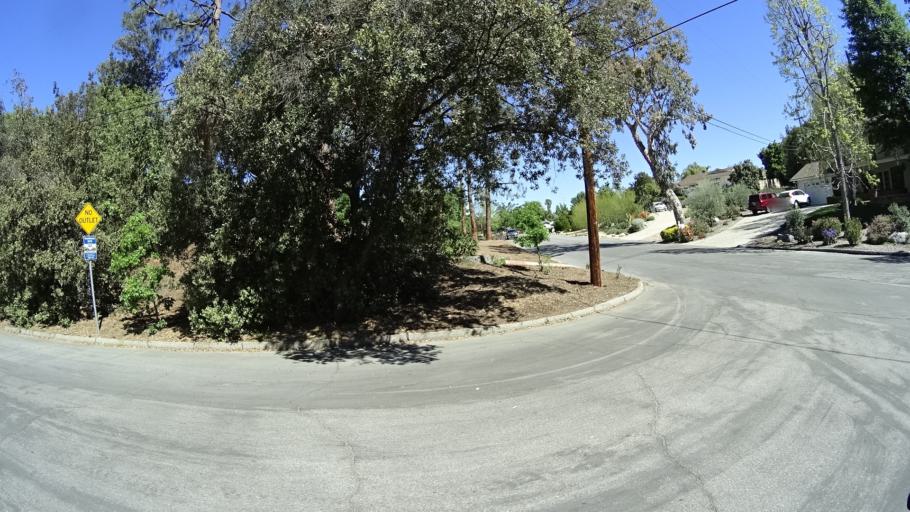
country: US
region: California
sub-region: Ventura County
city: Thousand Oaks
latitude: 34.1908
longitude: -118.8503
